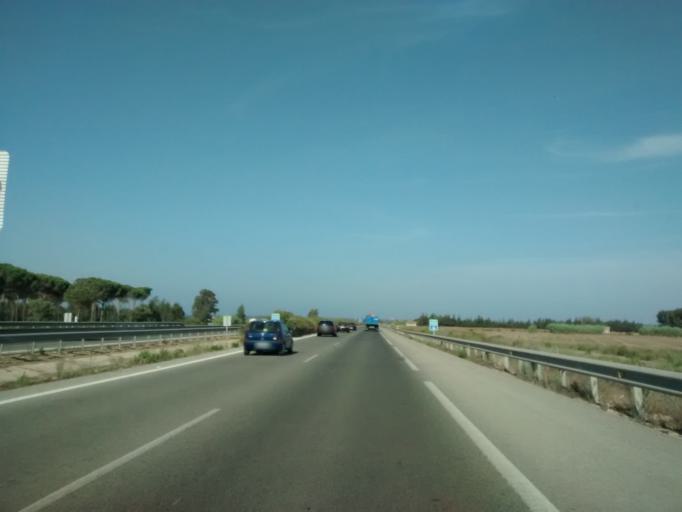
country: ES
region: Andalusia
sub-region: Provincia de Cadiz
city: Conil de la Frontera
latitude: 36.3528
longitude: -6.0707
